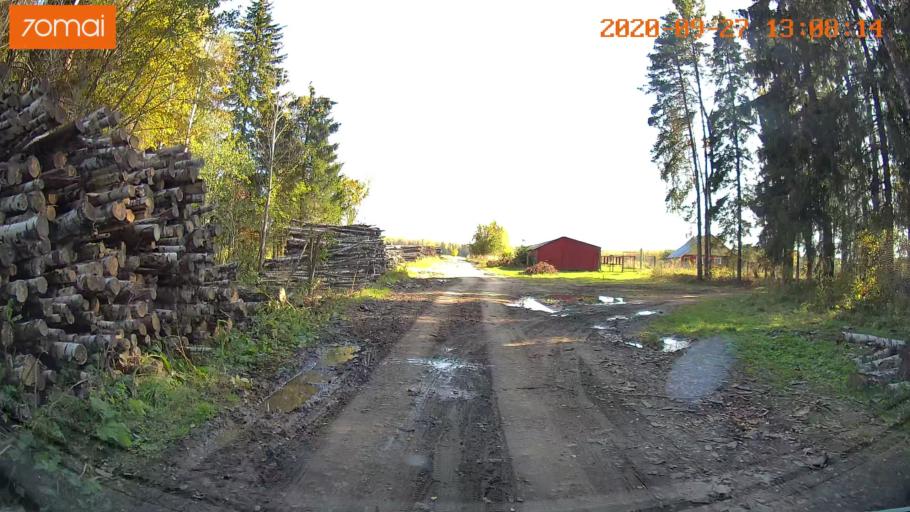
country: RU
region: Ivanovo
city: Furmanov
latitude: 57.1625
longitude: 41.0788
